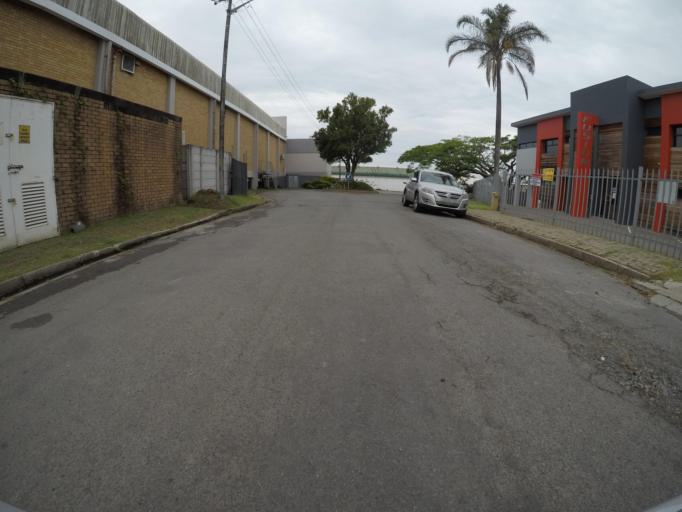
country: ZA
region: Eastern Cape
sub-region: Buffalo City Metropolitan Municipality
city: East London
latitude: -32.9819
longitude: 27.8999
